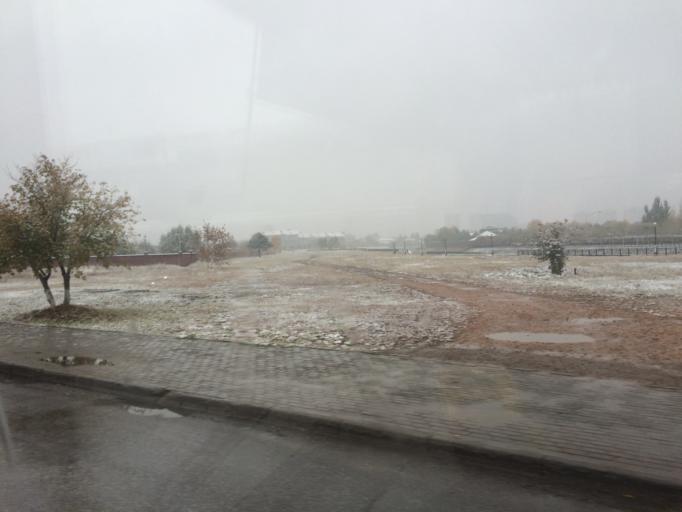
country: KZ
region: Astana Qalasy
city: Astana
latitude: 51.1496
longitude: 71.4445
